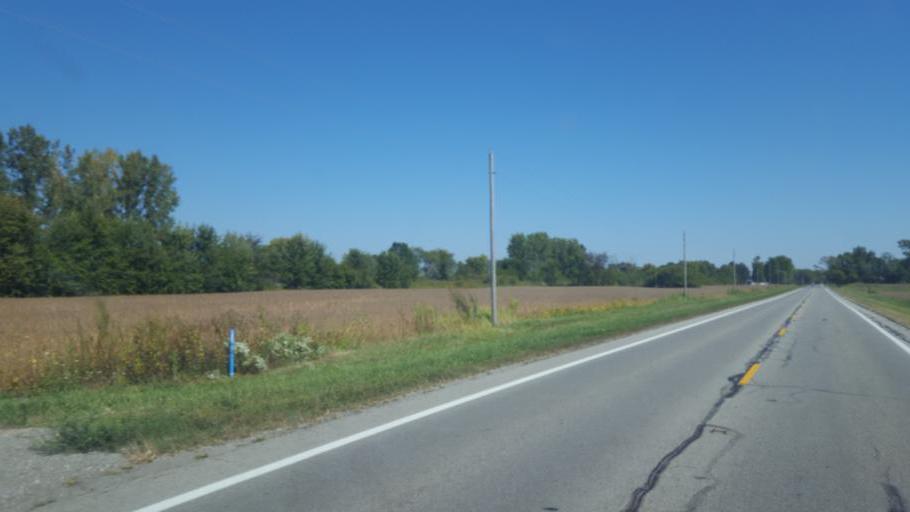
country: US
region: Ohio
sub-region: Marion County
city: Marion
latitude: 40.6270
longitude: -82.9976
